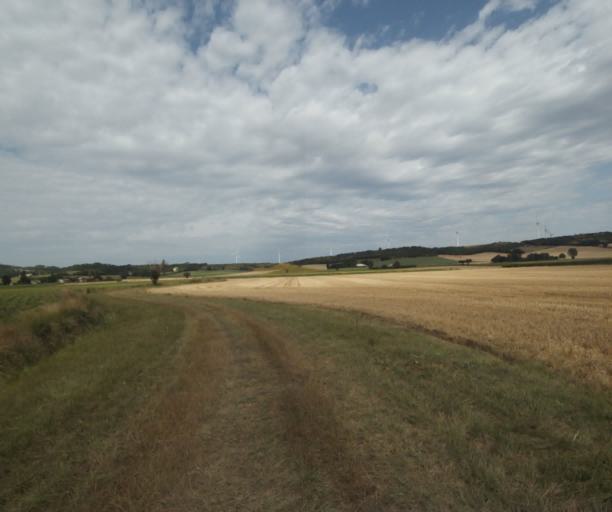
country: FR
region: Midi-Pyrenees
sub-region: Departement de la Haute-Garonne
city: Saint-Felix-Lauragais
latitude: 43.4506
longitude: 1.9261
